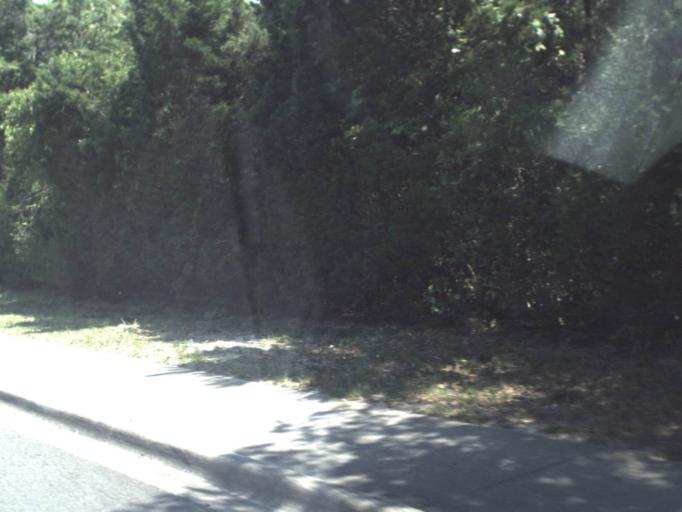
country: US
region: Florida
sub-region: Saint Johns County
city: Saint Augustine Beach
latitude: 29.8773
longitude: -81.2857
